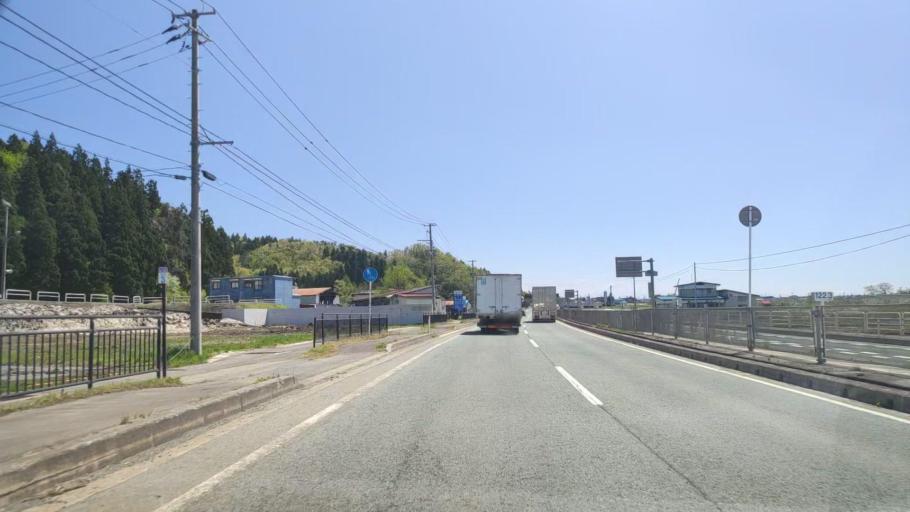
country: JP
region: Yamagata
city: Obanazawa
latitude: 38.5251
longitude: 140.3958
